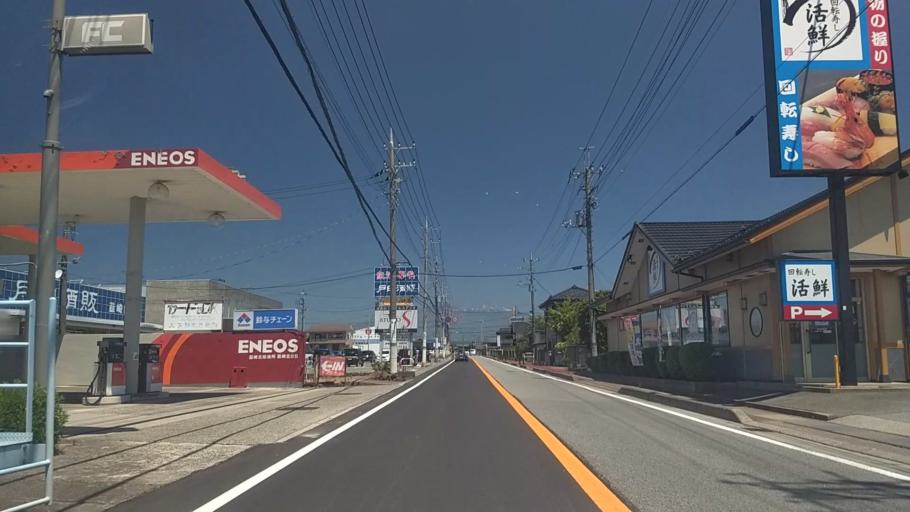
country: JP
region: Yamanashi
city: Nirasaki
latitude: 35.7226
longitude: 138.4505
